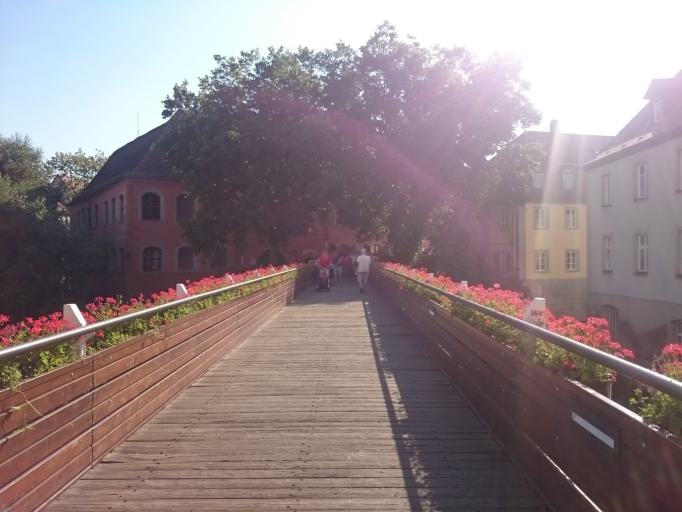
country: DE
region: Bavaria
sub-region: Upper Franconia
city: Bamberg
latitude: 49.8910
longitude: 10.8868
